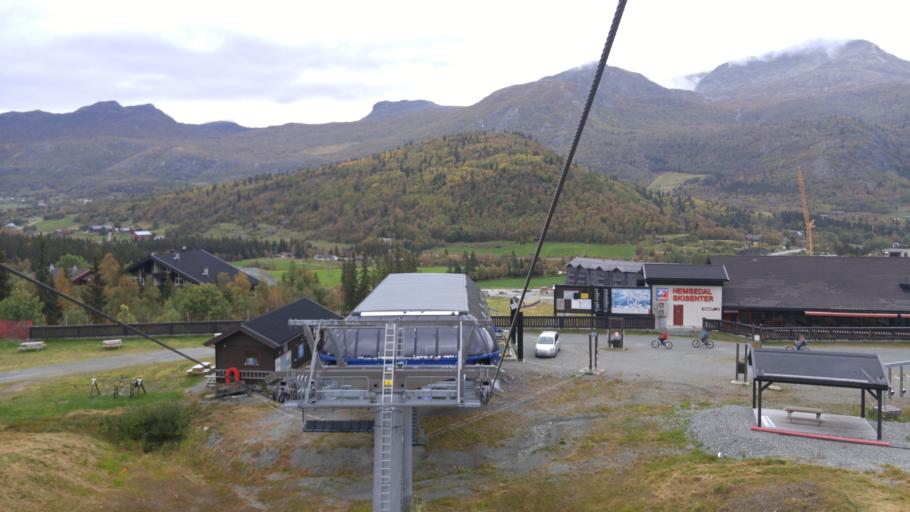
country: NO
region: Buskerud
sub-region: Hemsedal
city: Hemsedal
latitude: 60.8596
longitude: 8.5134
